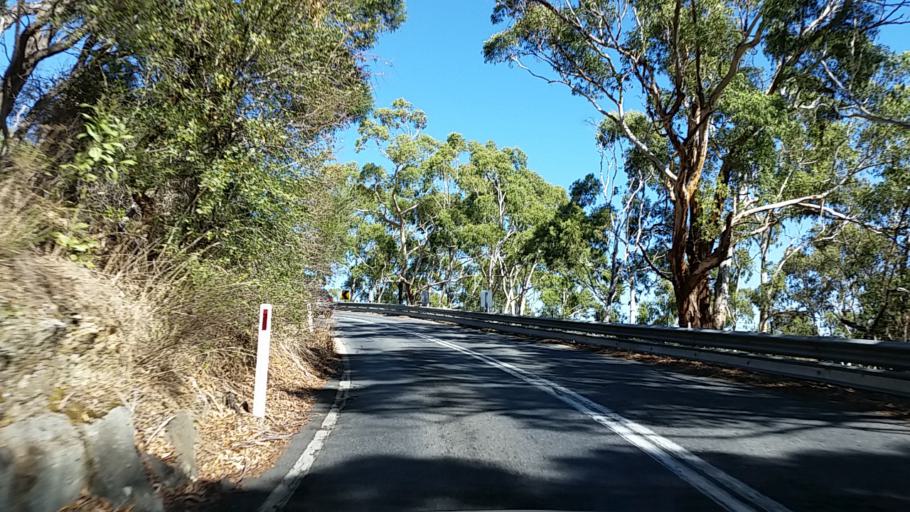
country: AU
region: South Australia
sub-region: Burnside
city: Beaumont
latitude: -34.9528
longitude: 138.6957
